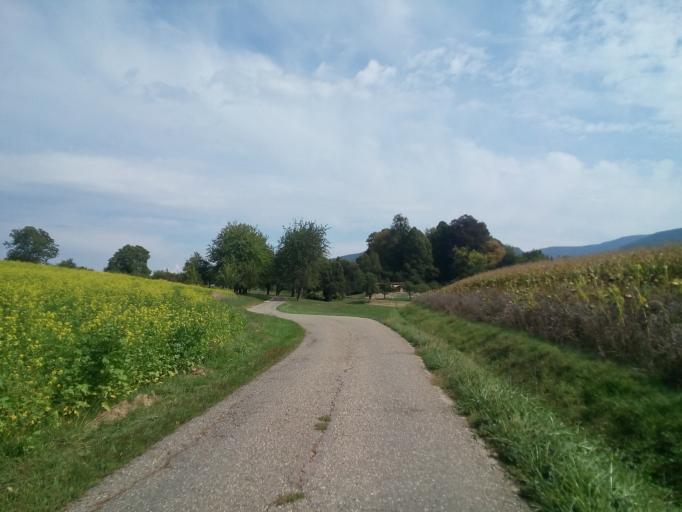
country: DE
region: Baden-Wuerttemberg
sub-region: Freiburg Region
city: Sasbach
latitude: 48.6498
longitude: 8.1020
